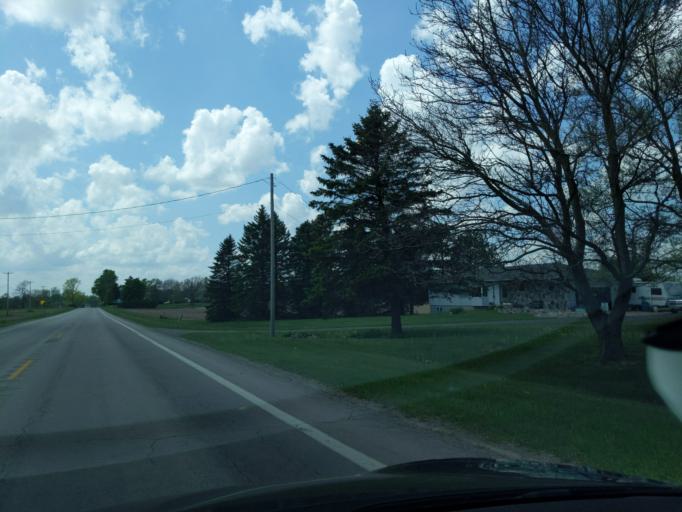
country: US
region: Michigan
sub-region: Ingham County
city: Mason
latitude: 42.5559
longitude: -84.3136
